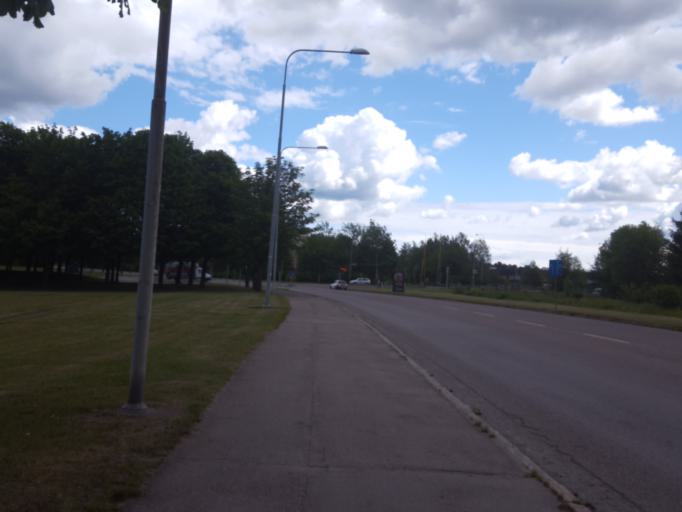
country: SE
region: Uppsala
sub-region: Uppsala Kommun
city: Saevja
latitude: 59.8592
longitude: 17.6849
